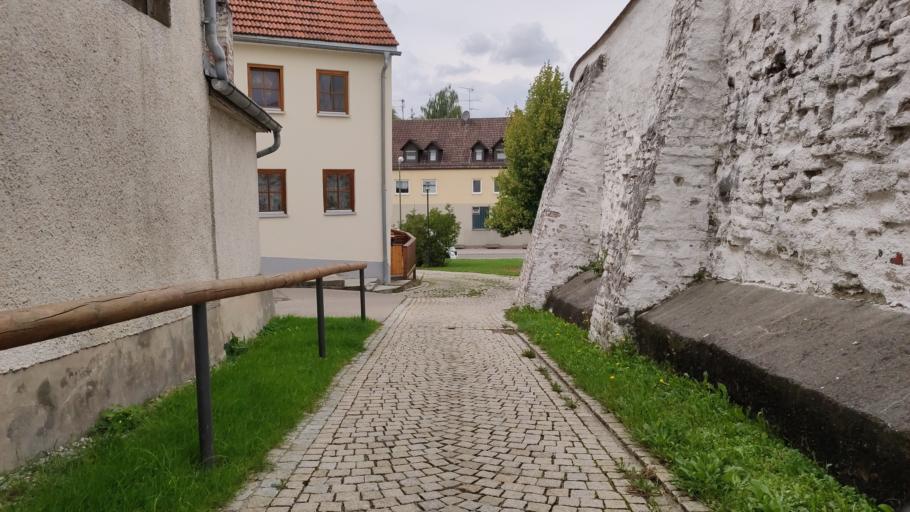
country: DE
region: Bavaria
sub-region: Swabia
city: Wehringen
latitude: 48.2455
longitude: 10.8013
